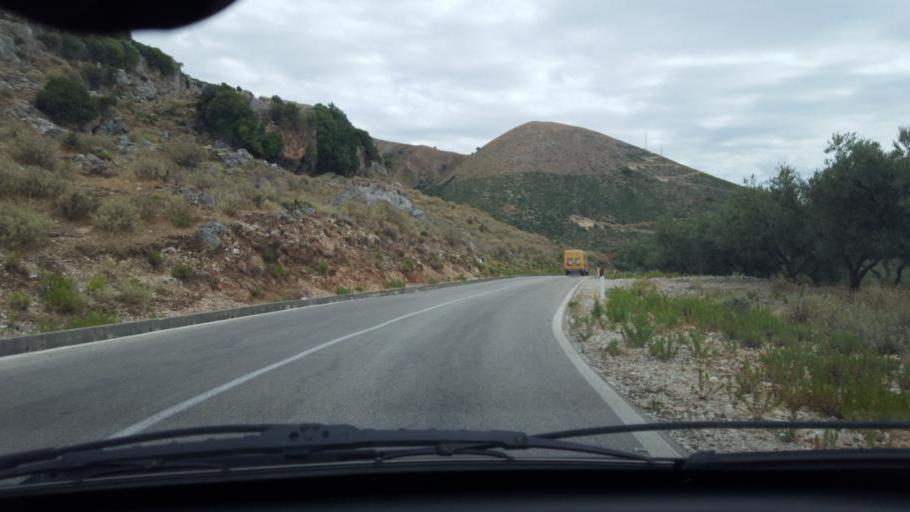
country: AL
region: Vlore
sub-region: Rrethi i Sarandes
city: Lukove
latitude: 40.0363
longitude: 19.8821
